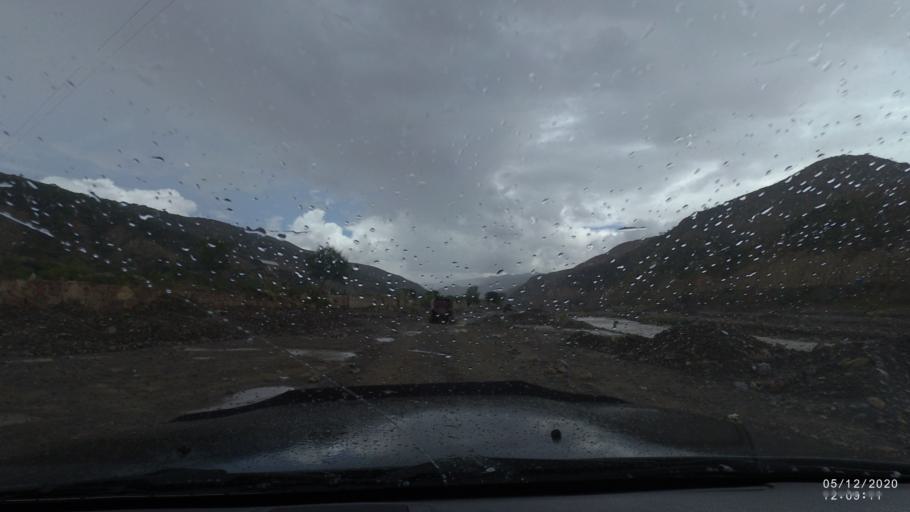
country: BO
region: Cochabamba
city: Sipe Sipe
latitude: -17.5695
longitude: -66.3694
